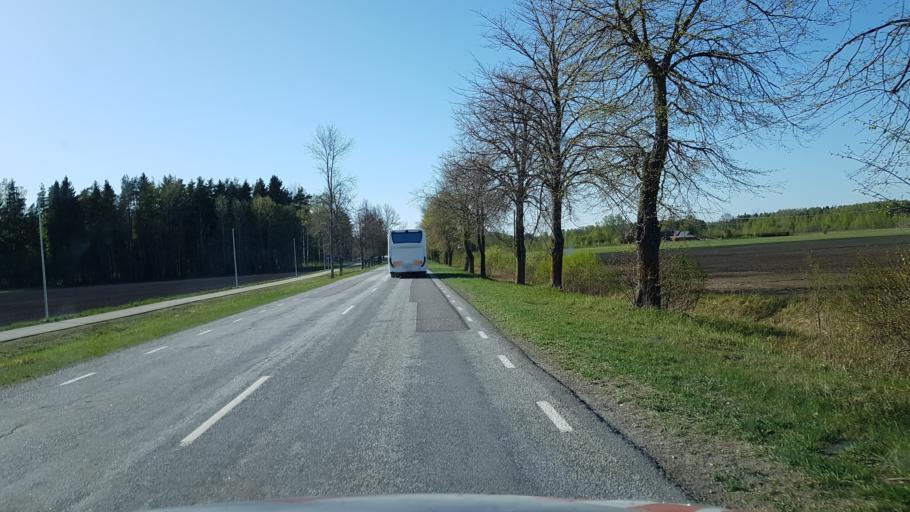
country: EE
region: Paernumaa
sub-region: Paikuse vald
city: Paikuse
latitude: 58.3627
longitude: 24.6489
